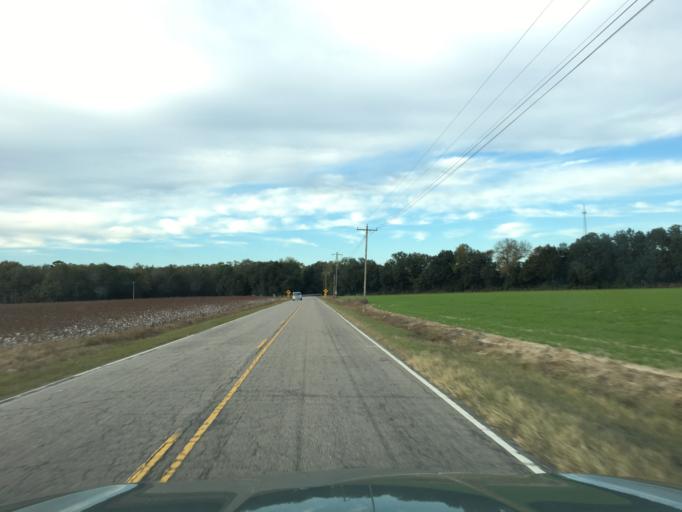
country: US
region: South Carolina
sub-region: Lexington County
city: Leesville
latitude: 33.7539
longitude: -81.3666
